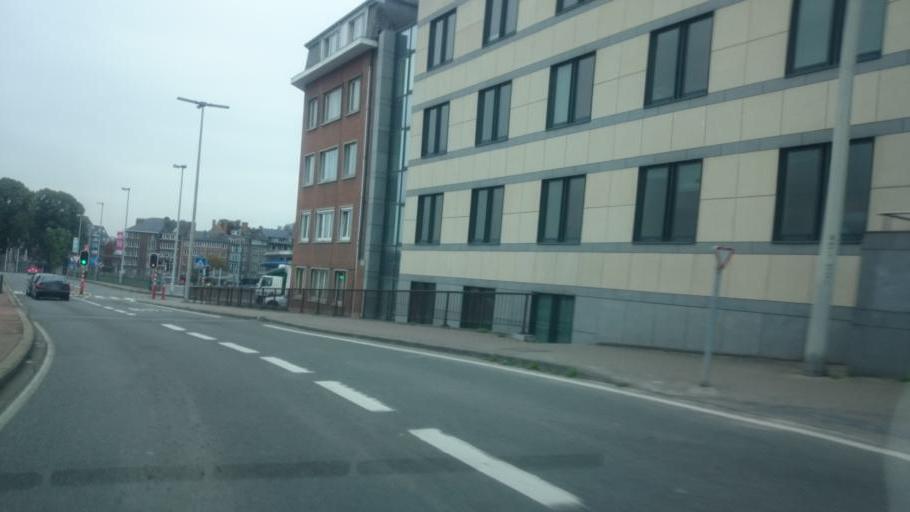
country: BE
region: Wallonia
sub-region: Province de Namur
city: Namur
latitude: 50.4707
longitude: 4.8677
